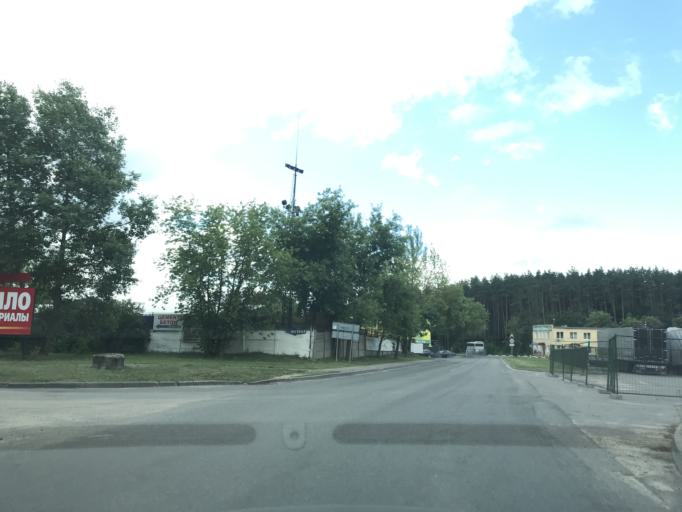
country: BY
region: Minsk
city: Borovlyany
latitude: 53.9590
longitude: 27.6907
